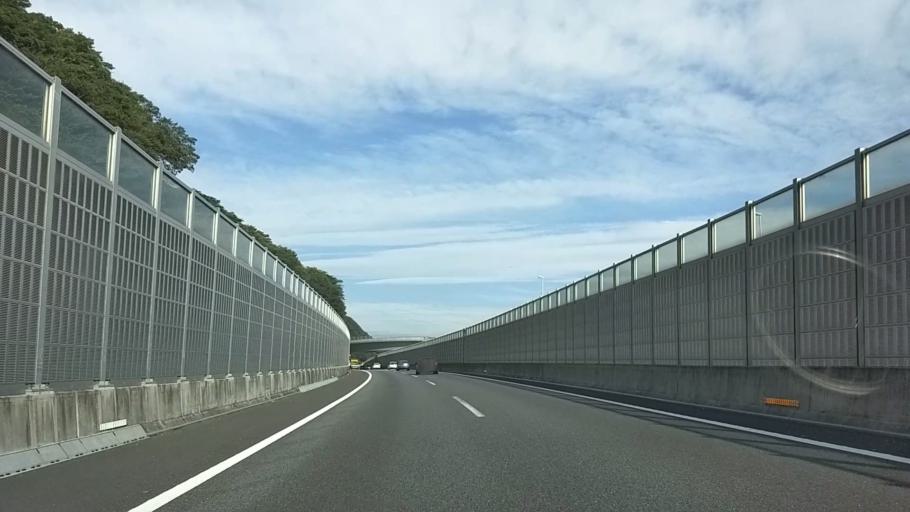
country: JP
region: Kanagawa
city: Zama
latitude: 35.5217
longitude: 139.3559
